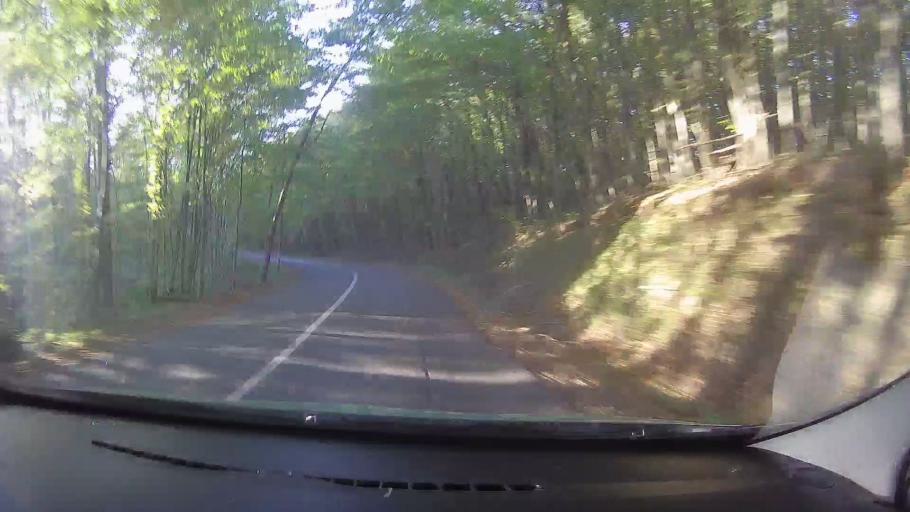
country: RO
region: Timis
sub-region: Comuna Nadrag
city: Nadrag
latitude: 45.6753
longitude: 22.1633
